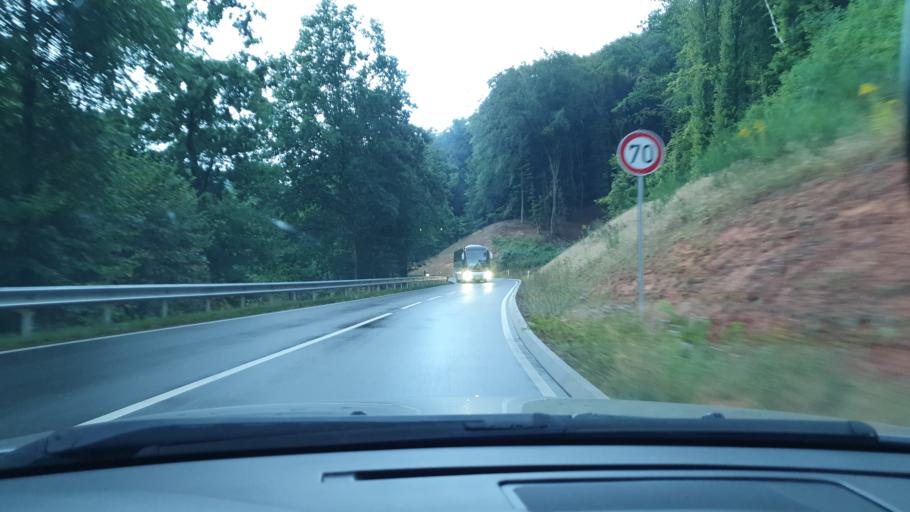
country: DE
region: Rheinland-Pfalz
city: Obernheim-Kirchenarnbach
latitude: 49.3497
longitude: 7.5717
